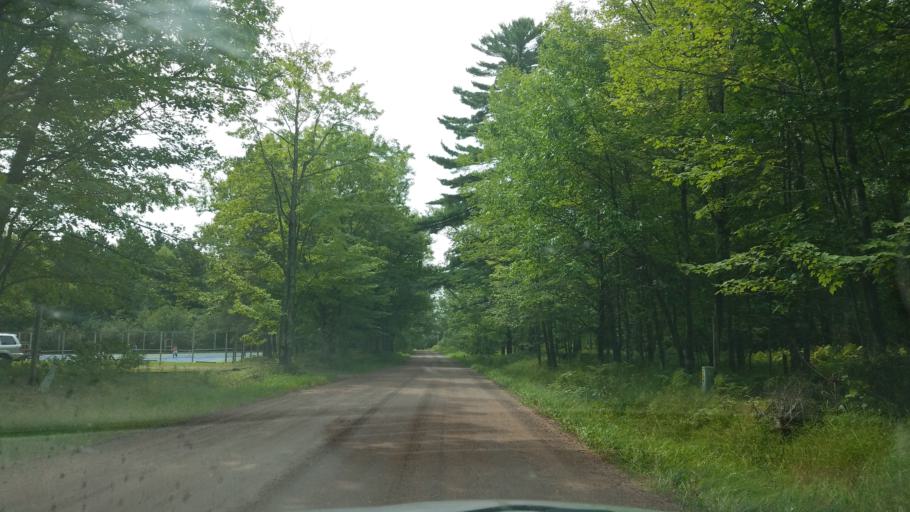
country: US
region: Wisconsin
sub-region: Bayfield County
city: Washburn
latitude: 46.7588
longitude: -90.7831
